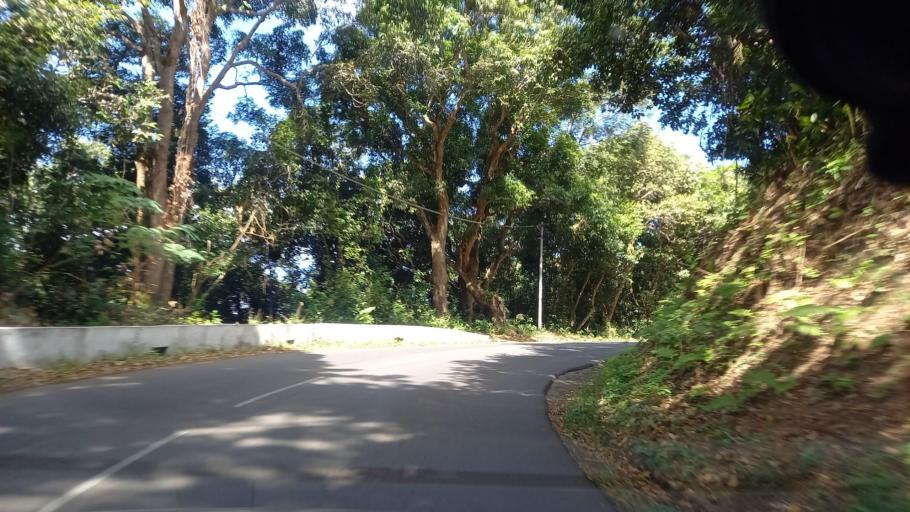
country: YT
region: Dembeni
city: Dembeni
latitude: -12.7871
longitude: 45.1653
